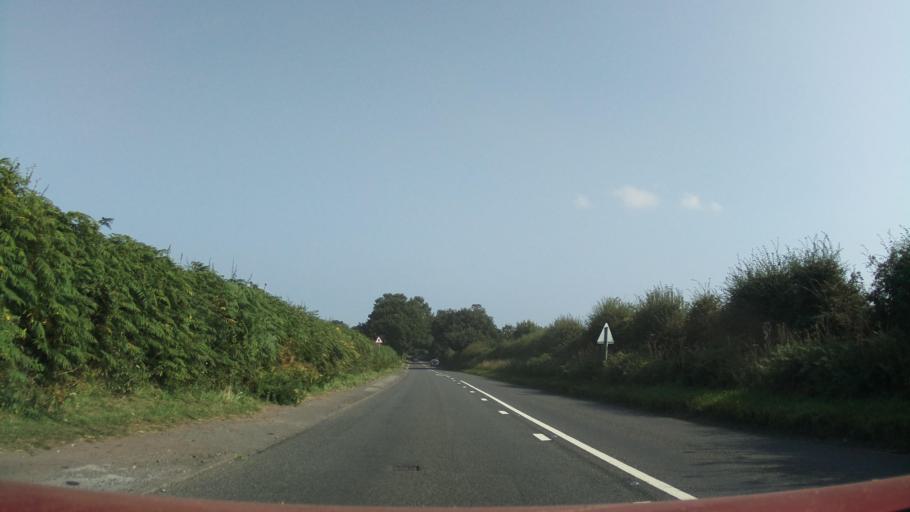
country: GB
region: England
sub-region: Staffordshire
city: Shenstone
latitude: 52.6609
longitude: -1.8758
